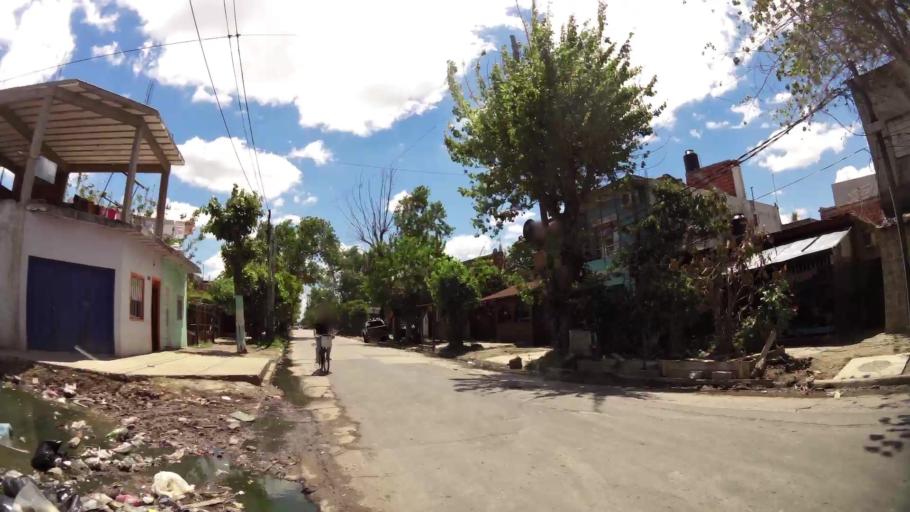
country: AR
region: Buenos Aires
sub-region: Partido de Lanus
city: Lanus
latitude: -34.7148
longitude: -58.4331
